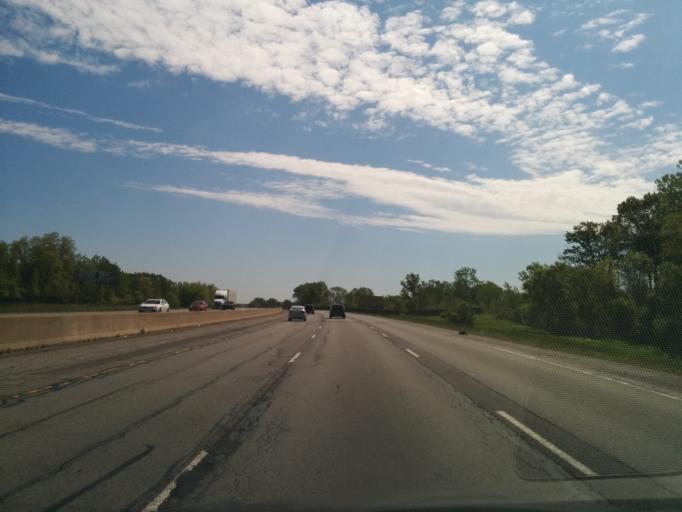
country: US
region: Indiana
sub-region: Porter County
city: Burns Harbor
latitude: 41.6020
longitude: -87.1463
